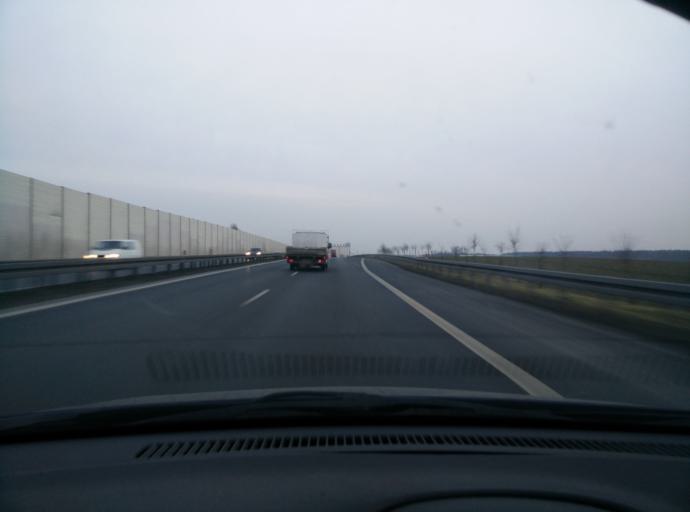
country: PL
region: Greater Poland Voivodeship
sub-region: Powiat poznanski
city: Kornik
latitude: 52.3163
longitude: 17.0412
